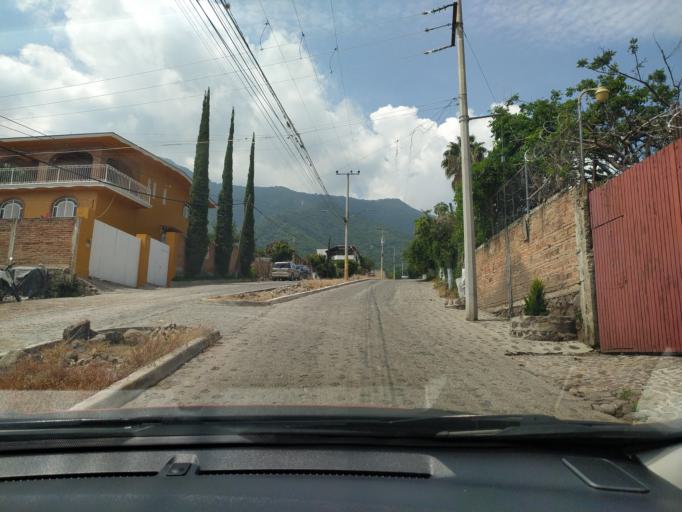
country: MX
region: Jalisco
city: San Juan Cosala
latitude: 20.2868
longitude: -103.3333
